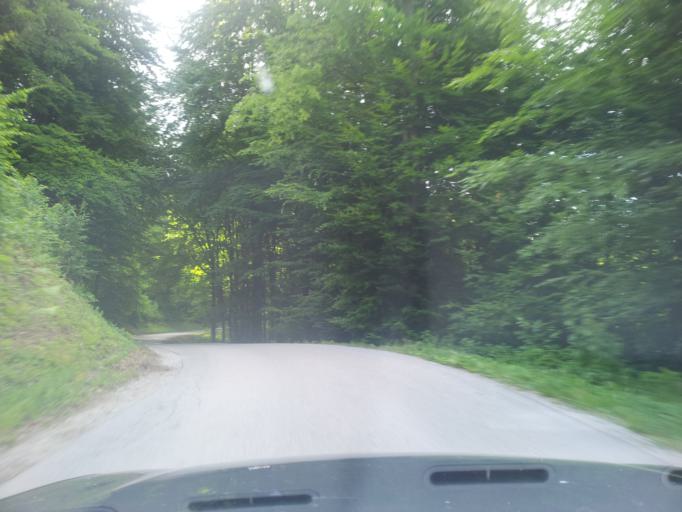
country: HR
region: Karlovacka
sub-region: Grad Karlovac
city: Karlovac
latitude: 45.4718
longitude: 15.4774
